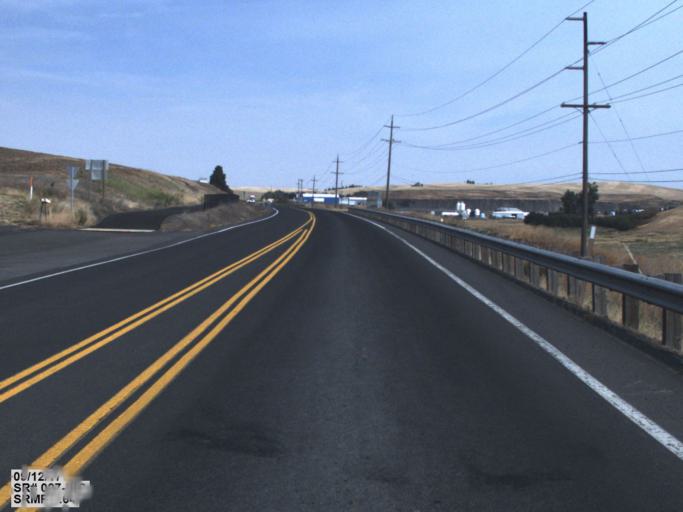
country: US
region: Washington
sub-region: Whitman County
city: Pullman
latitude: 46.7521
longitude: -117.1708
